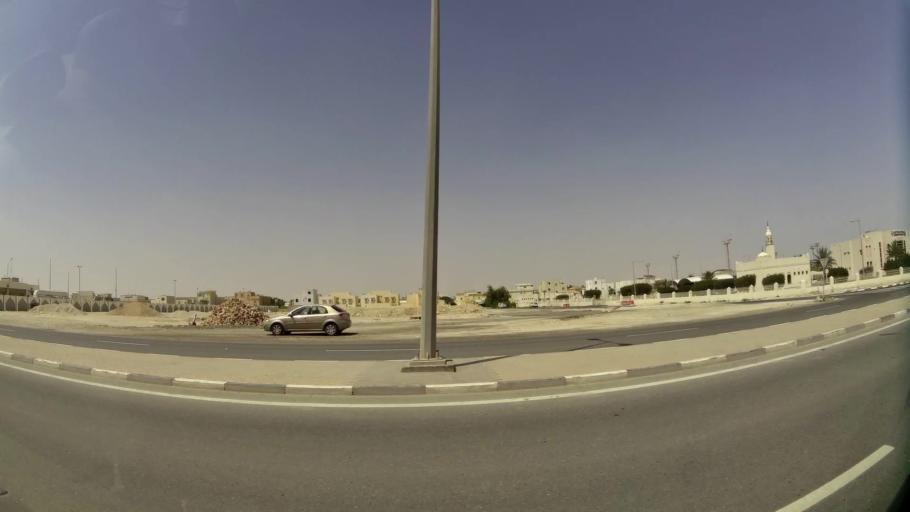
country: QA
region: Baladiyat Umm Salal
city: Umm Salal Muhammad
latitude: 25.3765
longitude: 51.4346
